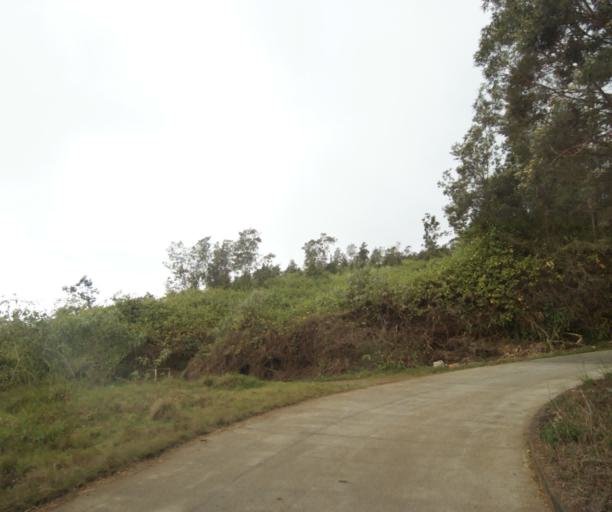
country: RE
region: Reunion
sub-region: Reunion
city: La Possession
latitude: -21.0111
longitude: 55.3554
